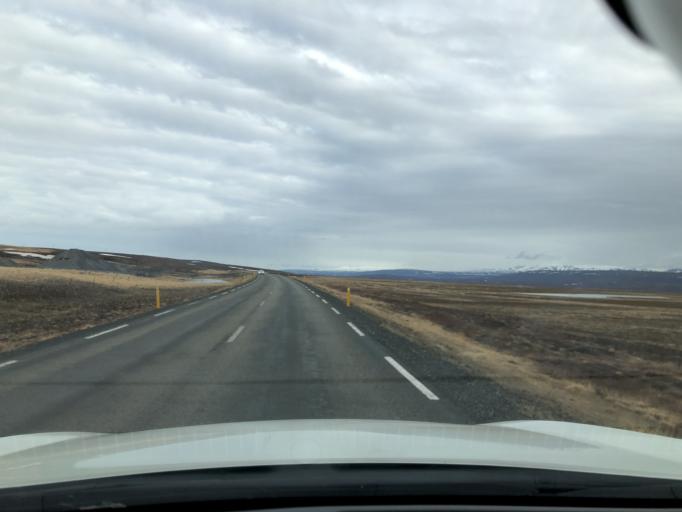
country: IS
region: Northeast
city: Laugar
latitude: 65.7125
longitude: -17.4735
